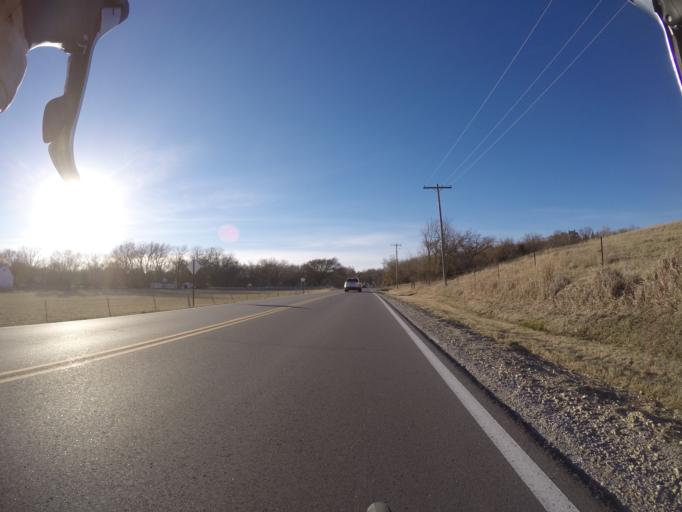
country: US
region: Kansas
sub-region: Riley County
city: Ogden
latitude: 39.2226
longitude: -96.7045
